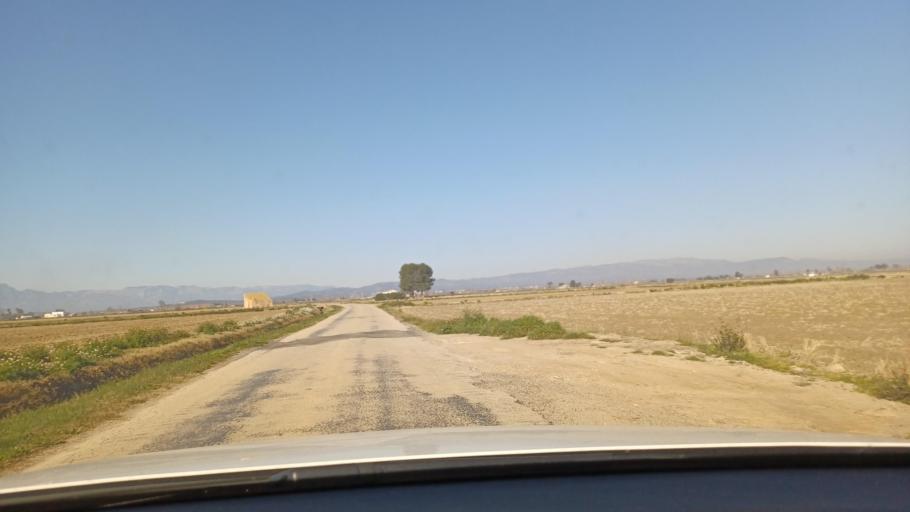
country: ES
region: Catalonia
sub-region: Provincia de Tarragona
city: Deltebre
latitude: 40.6945
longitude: 0.6505
